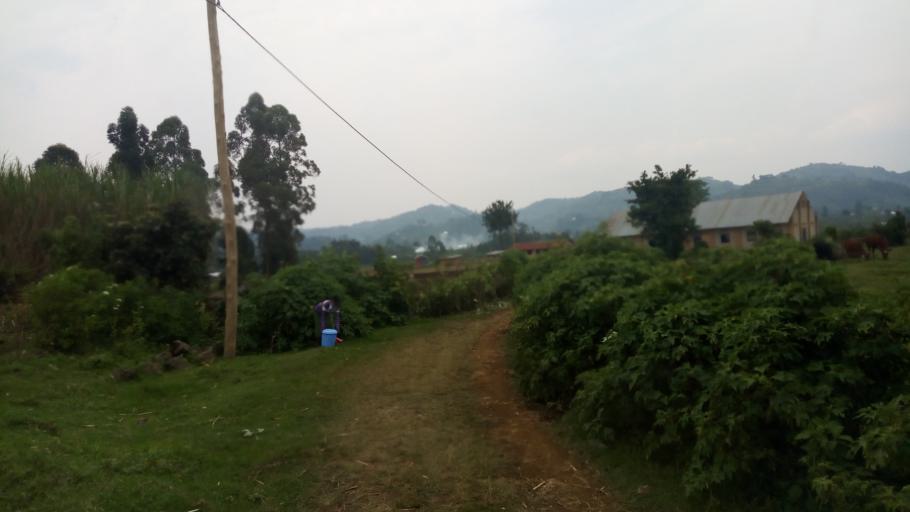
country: UG
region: Western Region
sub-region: Kisoro District
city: Kisoro
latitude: -1.2715
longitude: 29.6191
